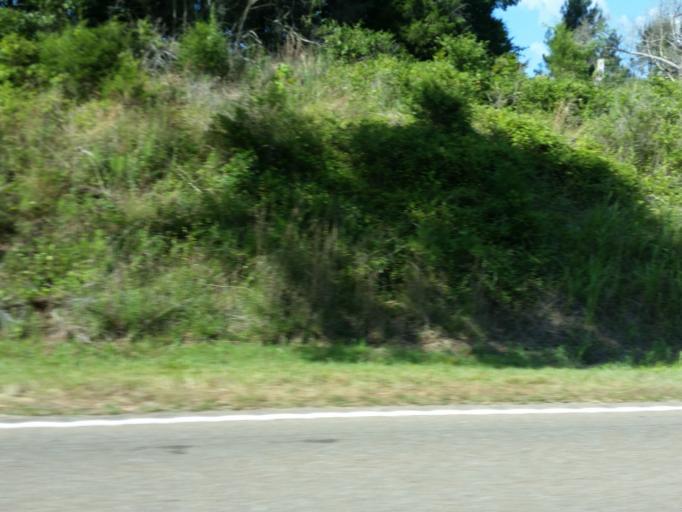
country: US
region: Tennessee
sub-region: Decatur County
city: Parsons
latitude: 35.6486
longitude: -88.1133
